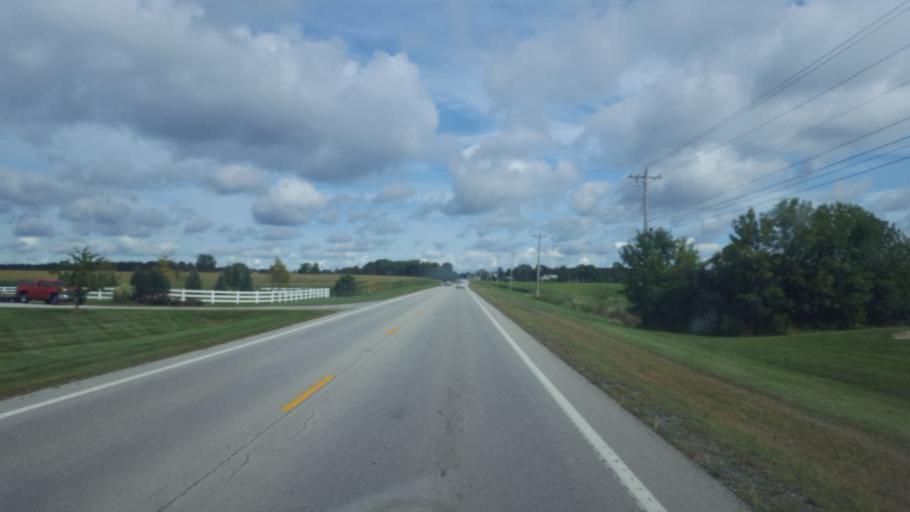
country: US
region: Ohio
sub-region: Lorain County
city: Oberlin
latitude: 41.2537
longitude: -82.2177
